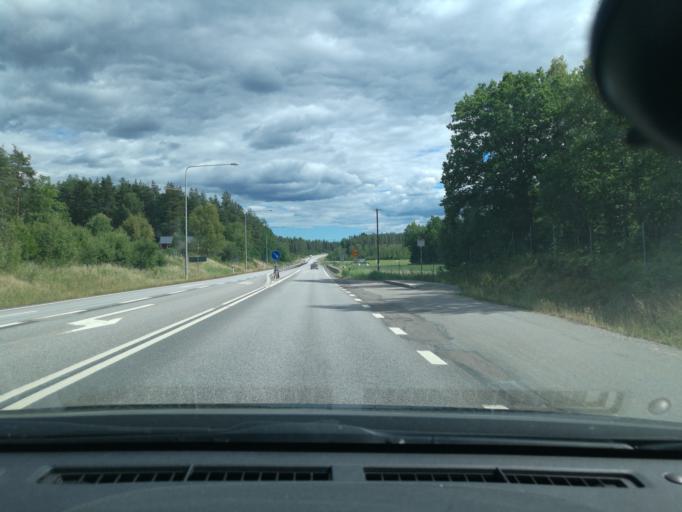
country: SE
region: OEstergoetland
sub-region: Soderkopings Kommun
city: Soederkoeping
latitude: 58.4405
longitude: 16.3723
